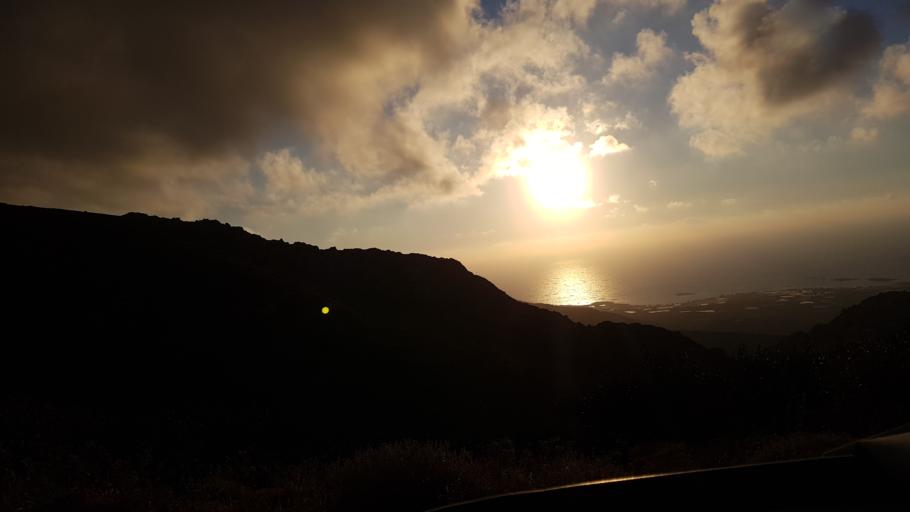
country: GR
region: Crete
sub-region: Nomos Chanias
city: Vryses
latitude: 35.4506
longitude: 23.6029
